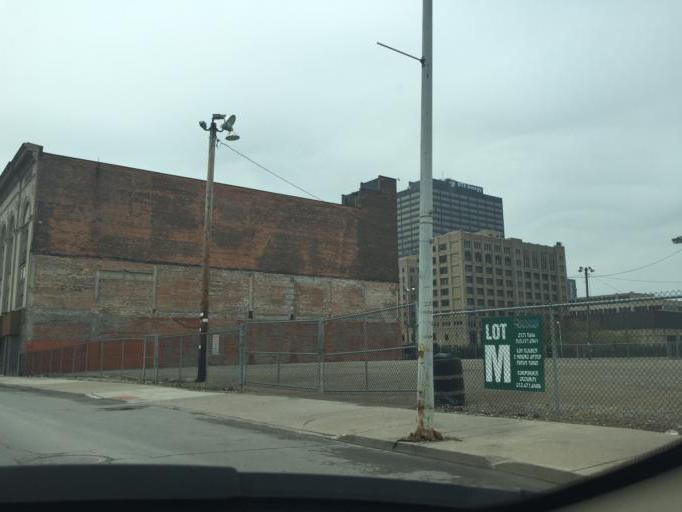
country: US
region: Michigan
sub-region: Wayne County
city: Detroit
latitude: 42.3367
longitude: -83.0557
